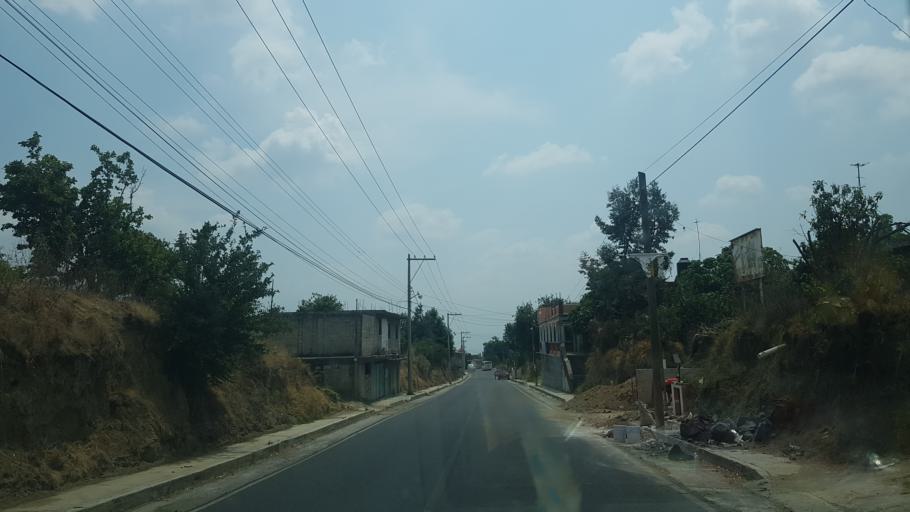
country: MX
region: Puebla
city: Domingo Arenas
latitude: 19.1407
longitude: -98.4647
